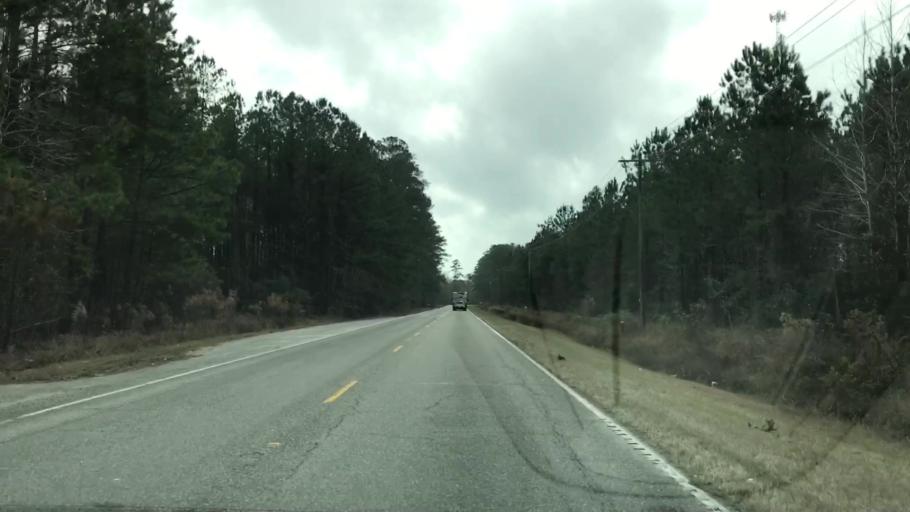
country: US
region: South Carolina
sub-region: Georgetown County
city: Murrells Inlet
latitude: 33.6245
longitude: -79.1913
